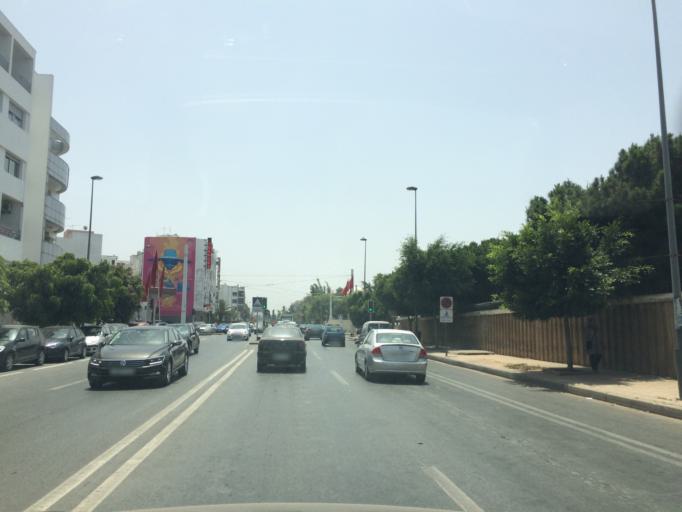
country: MA
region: Rabat-Sale-Zemmour-Zaer
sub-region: Rabat
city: Rabat
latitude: 33.9972
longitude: -6.8513
